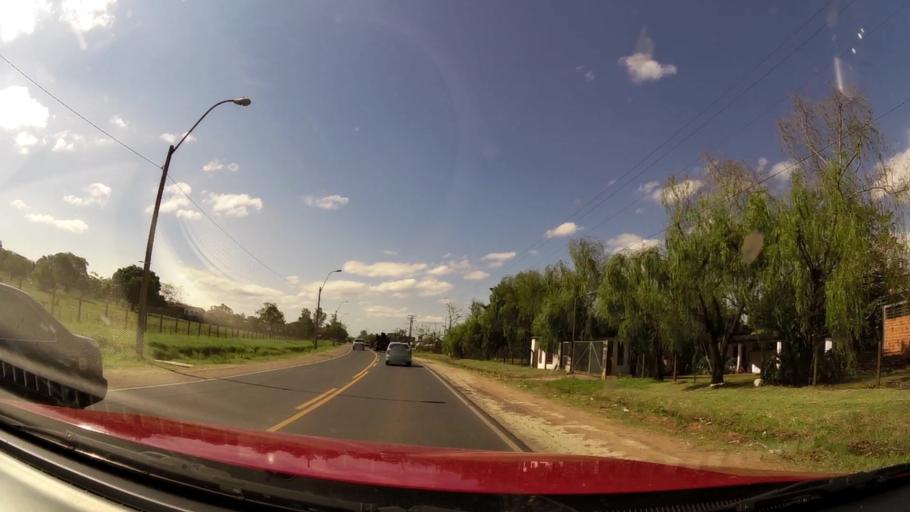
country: PY
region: Central
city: Fernando de la Mora
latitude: -25.2738
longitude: -57.5225
